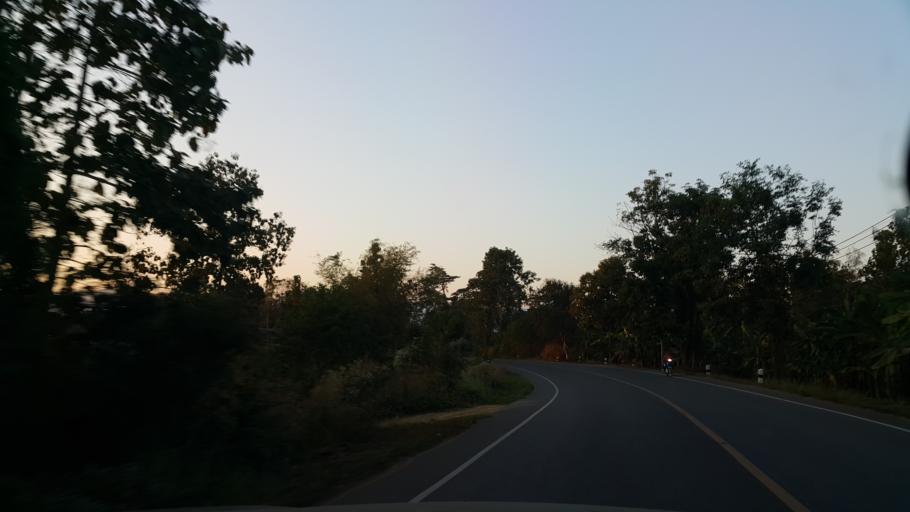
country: TH
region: Phrae
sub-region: Amphoe Wang Chin
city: Wang Chin
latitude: 17.8611
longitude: 99.6244
